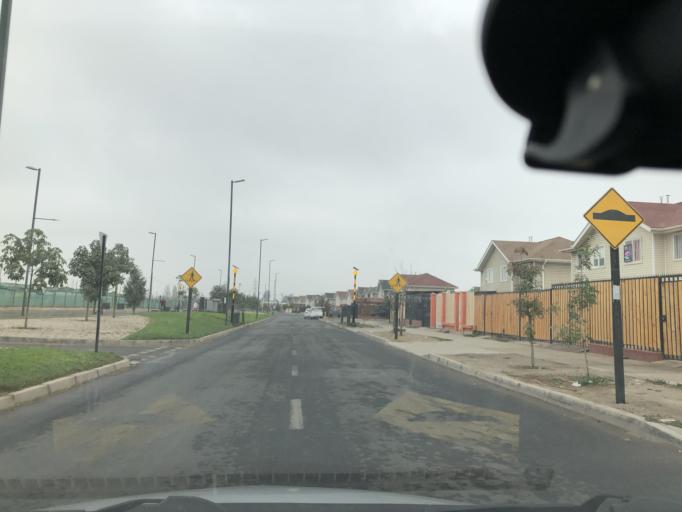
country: CL
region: Santiago Metropolitan
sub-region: Provincia de Cordillera
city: Puente Alto
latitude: -33.5967
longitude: -70.5968
